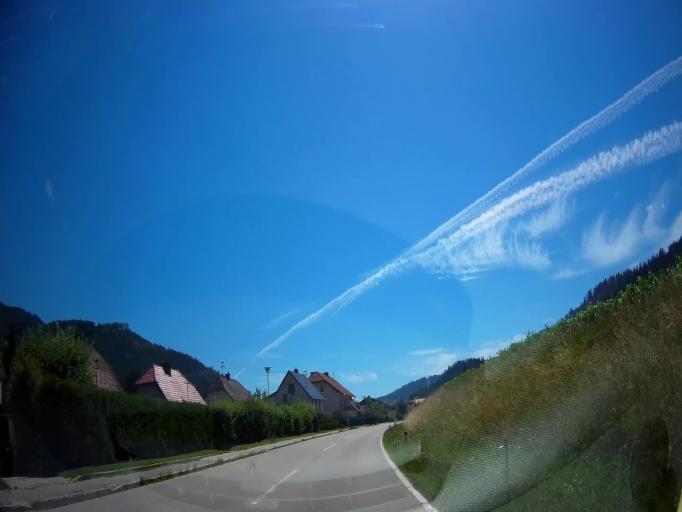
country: AT
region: Carinthia
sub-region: Politischer Bezirk Sankt Veit an der Glan
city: Micheldorf
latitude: 46.9115
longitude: 14.4333
